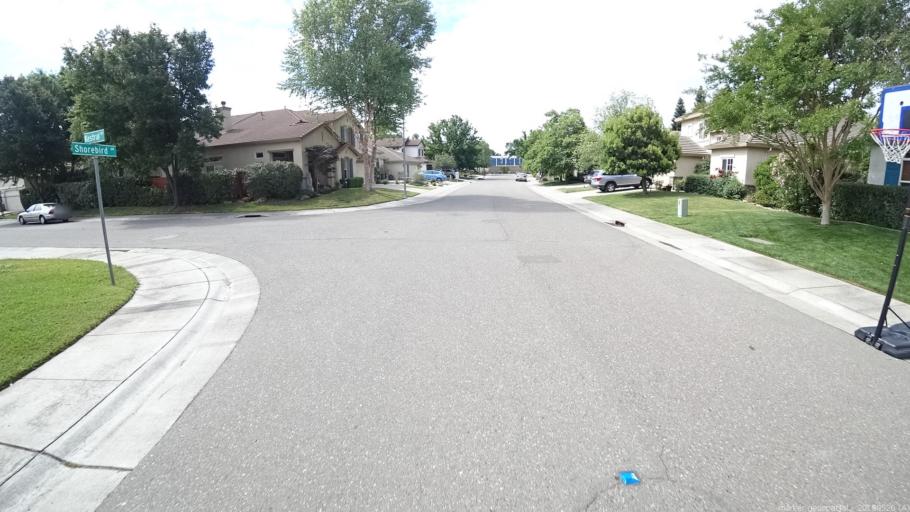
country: US
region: California
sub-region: Yolo County
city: West Sacramento
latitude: 38.6071
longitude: -121.5352
